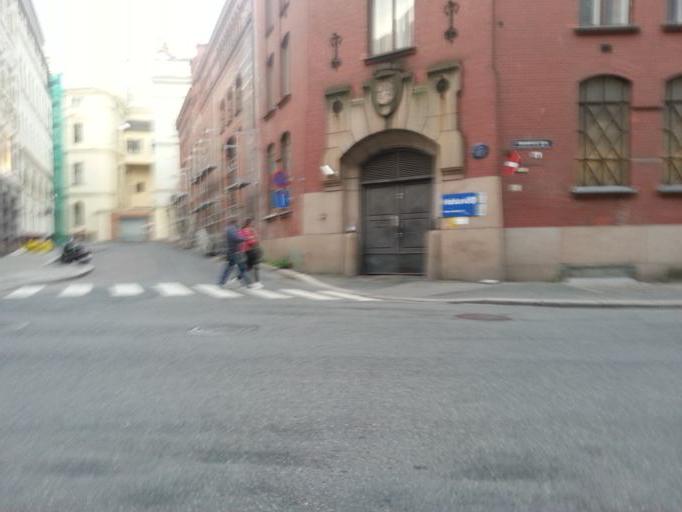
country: NO
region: Oslo
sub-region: Oslo
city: Oslo
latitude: 59.9127
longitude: 10.7373
